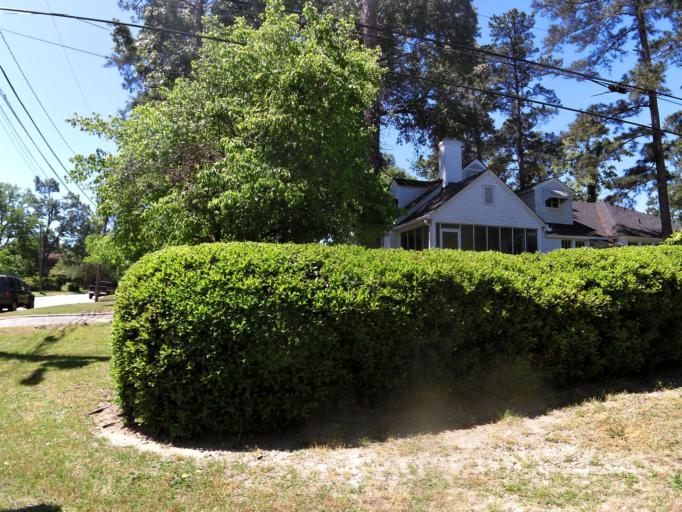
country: US
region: Georgia
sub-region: Columbia County
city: Martinez
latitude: 33.4810
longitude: -82.0355
